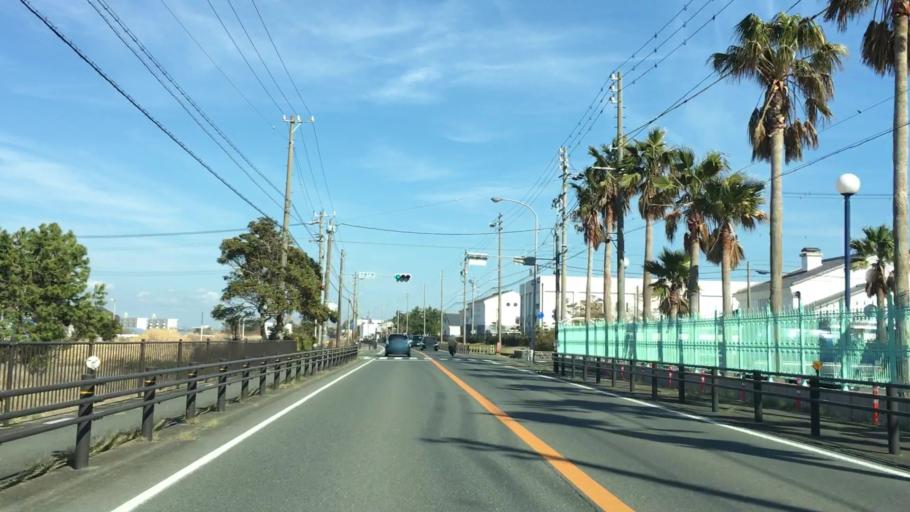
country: JP
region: Shizuoka
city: Kosai-shi
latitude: 34.6811
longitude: 137.5365
